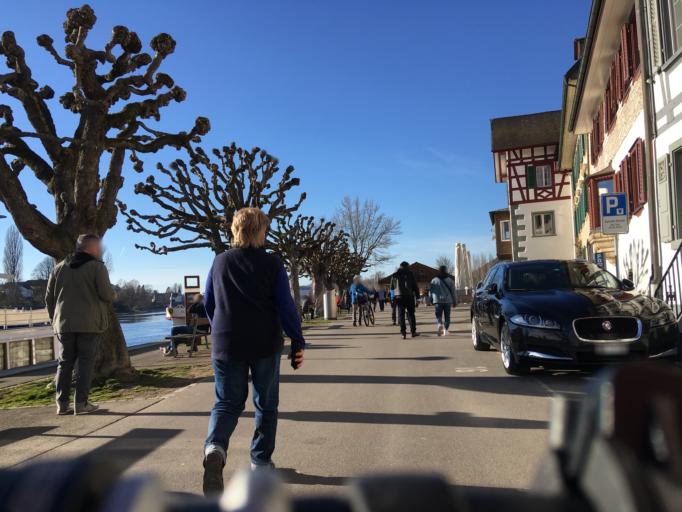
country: CH
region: Schaffhausen
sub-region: Bezirk Stein
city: Stein am Rhein
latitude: 47.6593
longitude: 8.8580
